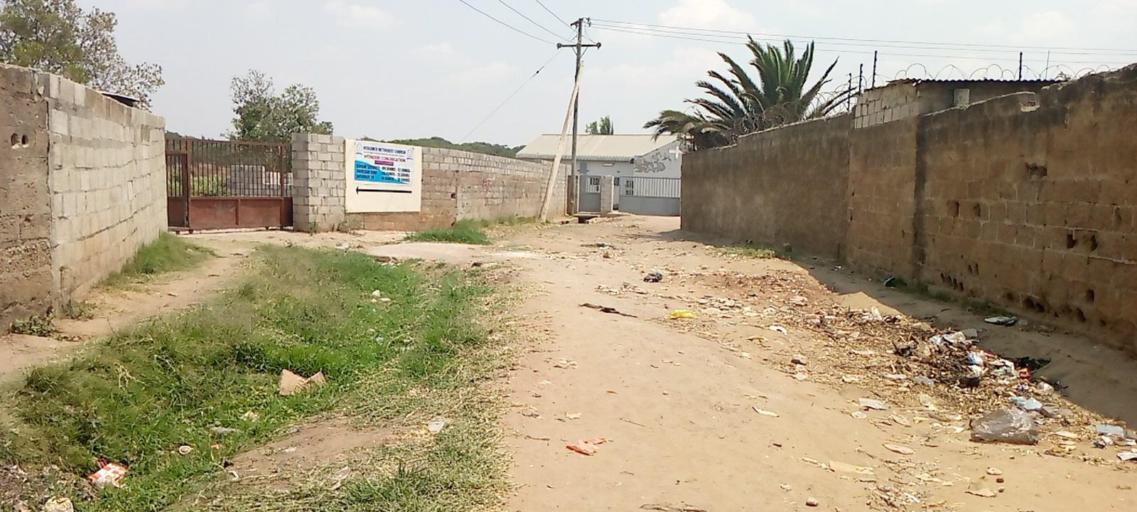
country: ZM
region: Lusaka
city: Lusaka
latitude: -15.3997
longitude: 28.3460
